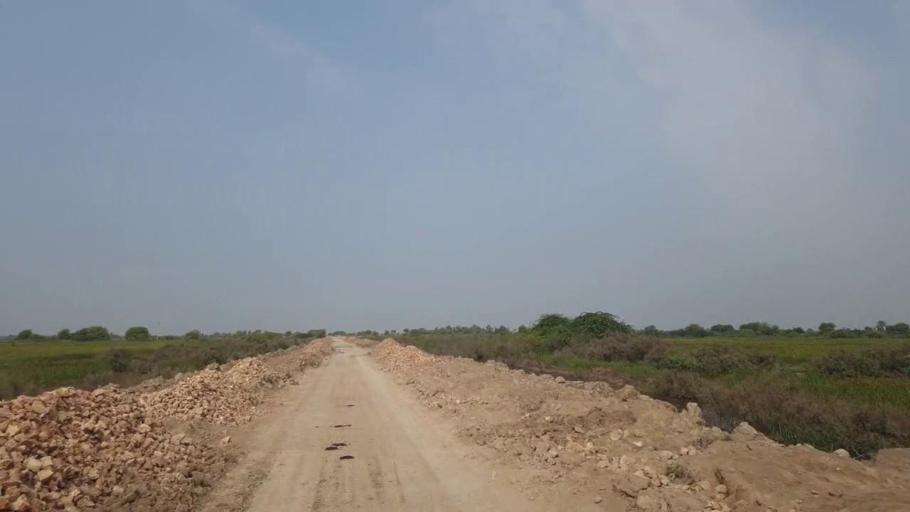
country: PK
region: Sindh
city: Badin
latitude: 24.6079
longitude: 68.7416
